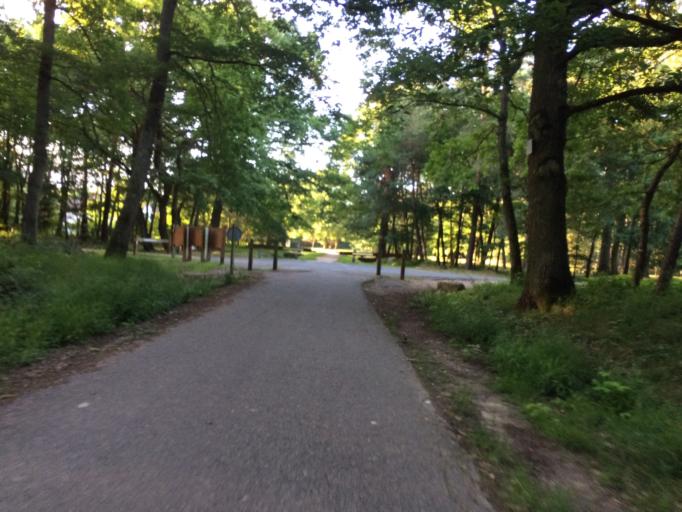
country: FR
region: Ile-de-France
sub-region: Departement de l'Essonne
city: Montgeron
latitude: 48.6854
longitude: 2.4662
